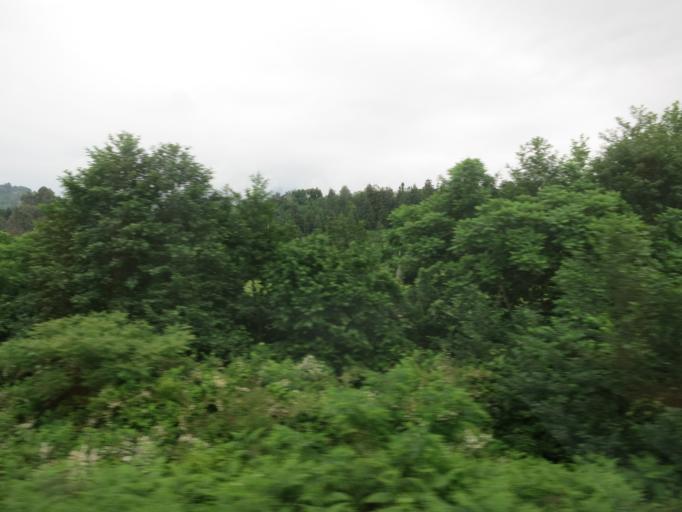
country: GE
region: Ajaria
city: Kobuleti
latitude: 41.7462
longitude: 41.7392
